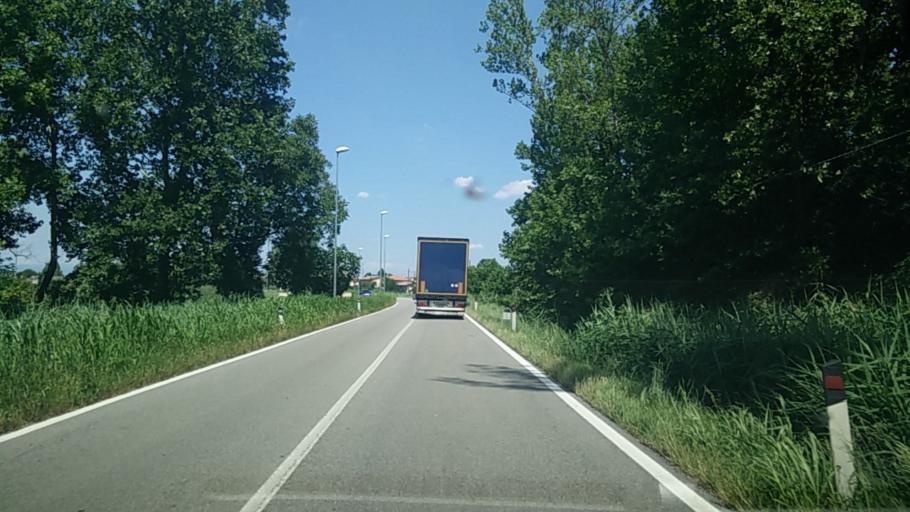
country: IT
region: Veneto
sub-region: Provincia di Padova
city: Tombolo
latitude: 45.6263
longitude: 11.8148
